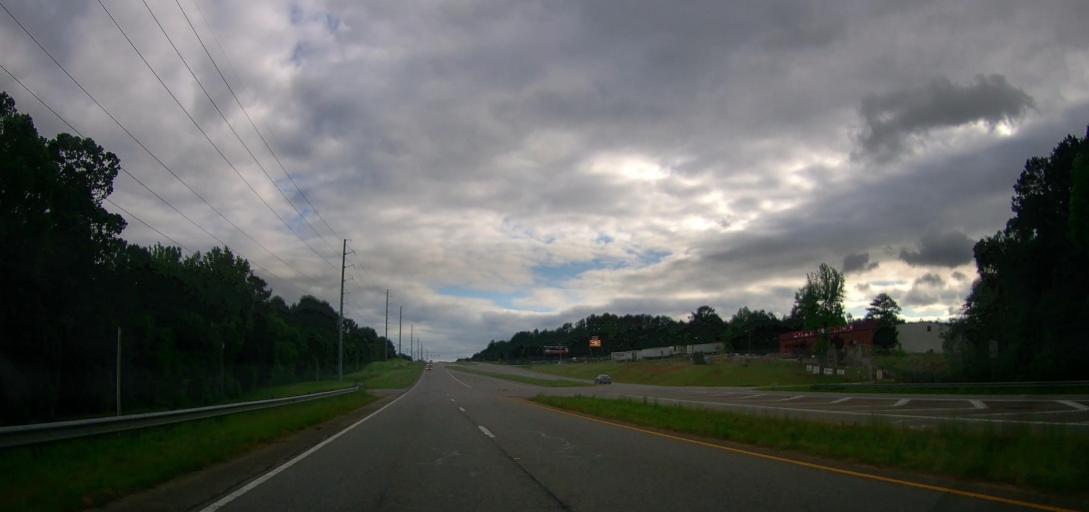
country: US
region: Georgia
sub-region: Oconee County
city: Bogart
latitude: 33.9312
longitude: -83.5083
